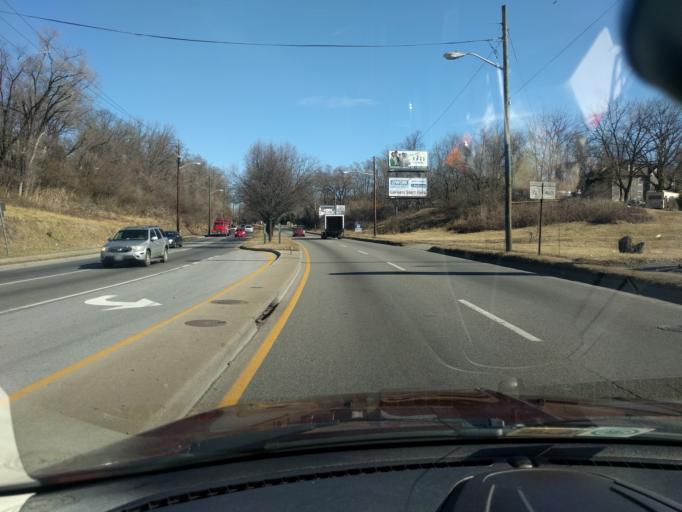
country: US
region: Virginia
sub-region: Roanoke County
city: Vinton
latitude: 37.2843
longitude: -79.9189
